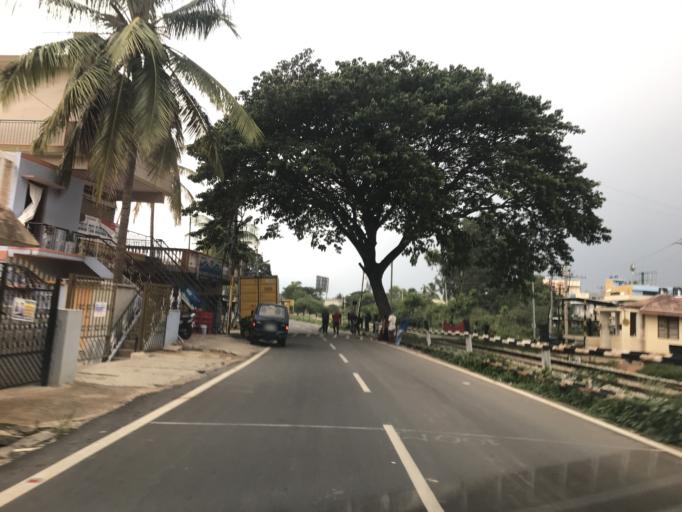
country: IN
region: Karnataka
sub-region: Bangalore Urban
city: Yelahanka
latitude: 13.1806
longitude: 77.6426
